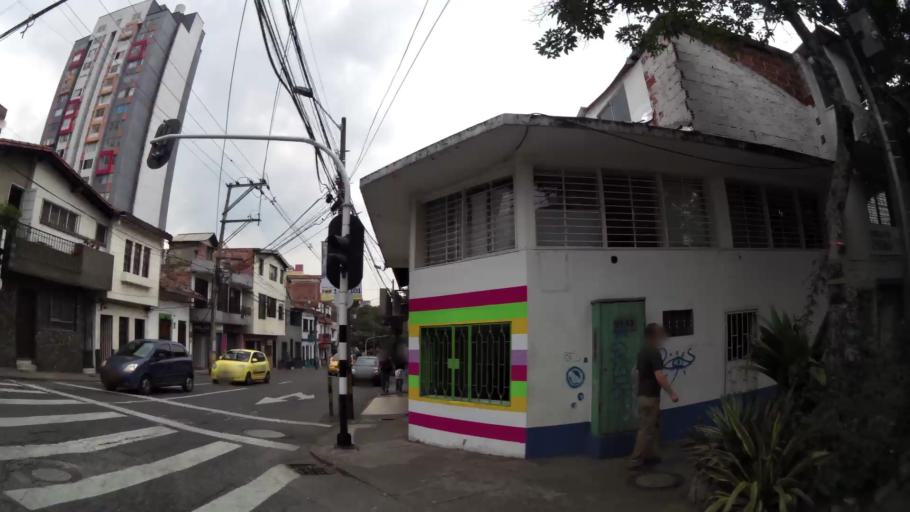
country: CO
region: Antioquia
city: Medellin
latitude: 6.2493
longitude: -75.5574
